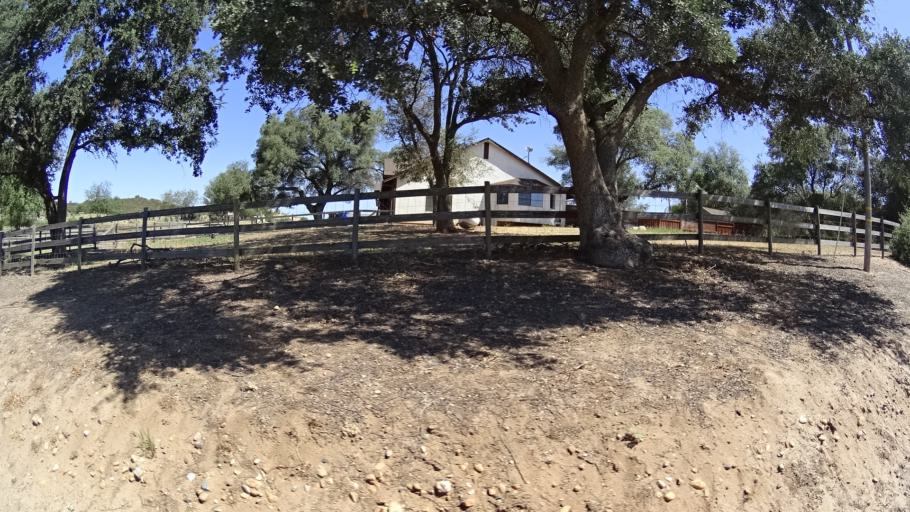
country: US
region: California
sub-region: Calaveras County
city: Rancho Calaveras
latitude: 38.1485
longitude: -120.9212
